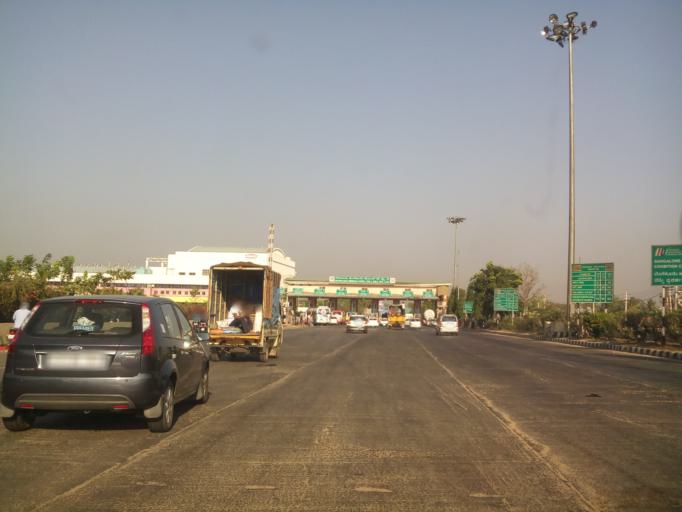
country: IN
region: Karnataka
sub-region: Bangalore Rural
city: Nelamangala
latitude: 13.0492
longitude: 77.4958
